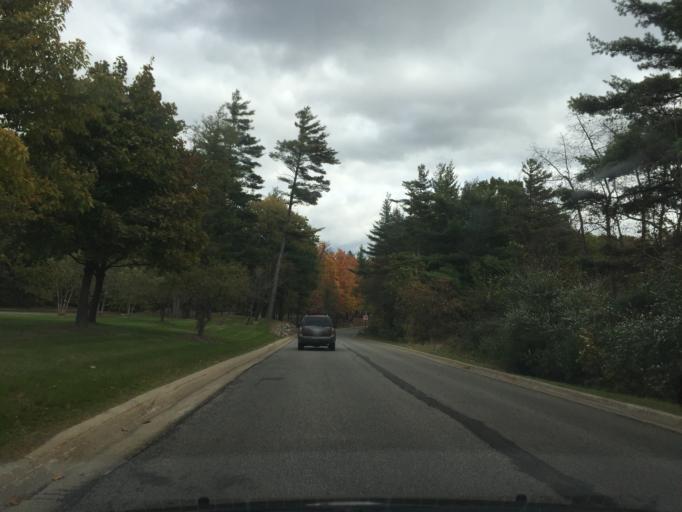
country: US
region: Michigan
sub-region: Oakland County
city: Auburn Hills
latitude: 42.6653
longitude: -83.2235
